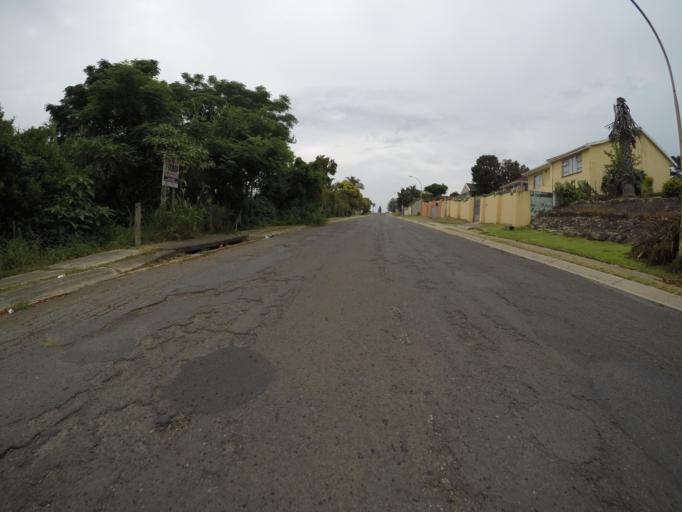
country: ZA
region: Eastern Cape
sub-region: Buffalo City Metropolitan Municipality
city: East London
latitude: -32.9965
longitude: 27.8595
